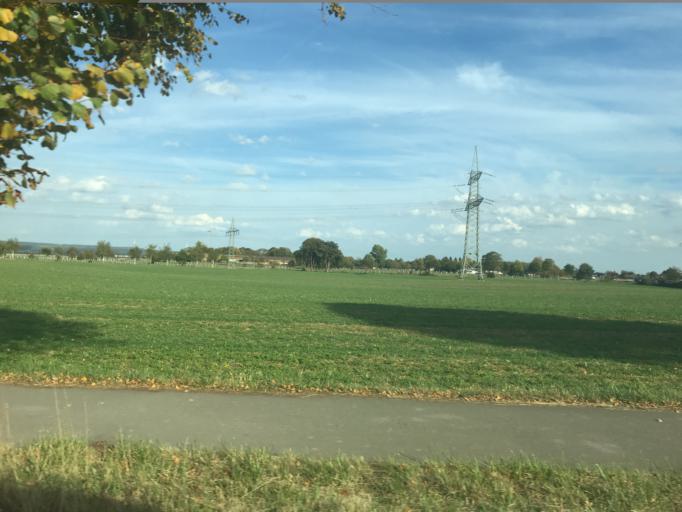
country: DE
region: North Rhine-Westphalia
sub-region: Regierungsbezirk Koln
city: Bergheim
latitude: 50.9145
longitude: 6.6181
